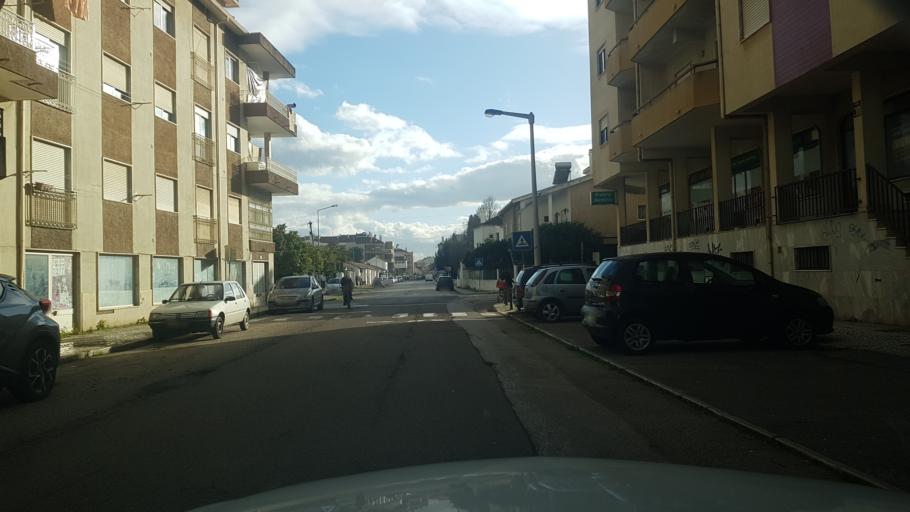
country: PT
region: Santarem
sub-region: Entroncamento
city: Entroncamento
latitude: 39.4706
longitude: -8.4730
